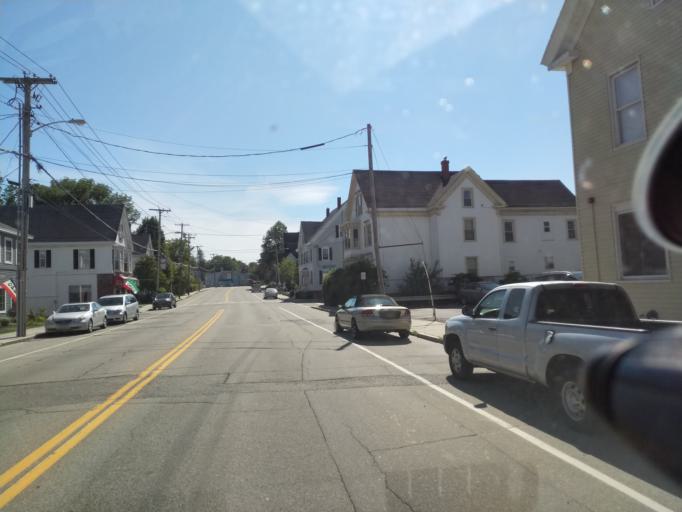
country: US
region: Maine
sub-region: Cumberland County
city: Westbrook
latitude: 43.6779
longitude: -70.3587
